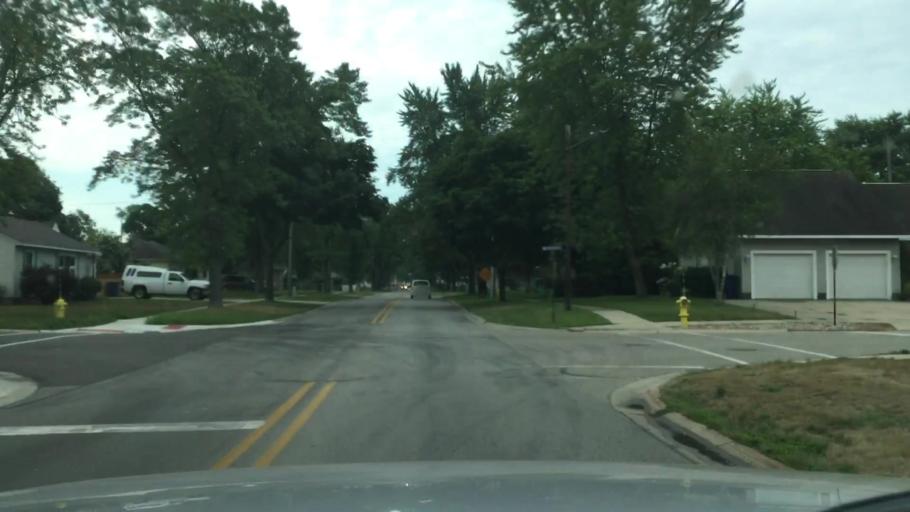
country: US
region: Michigan
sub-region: Muskegon County
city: Roosevelt Park
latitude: 43.2017
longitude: -86.2783
